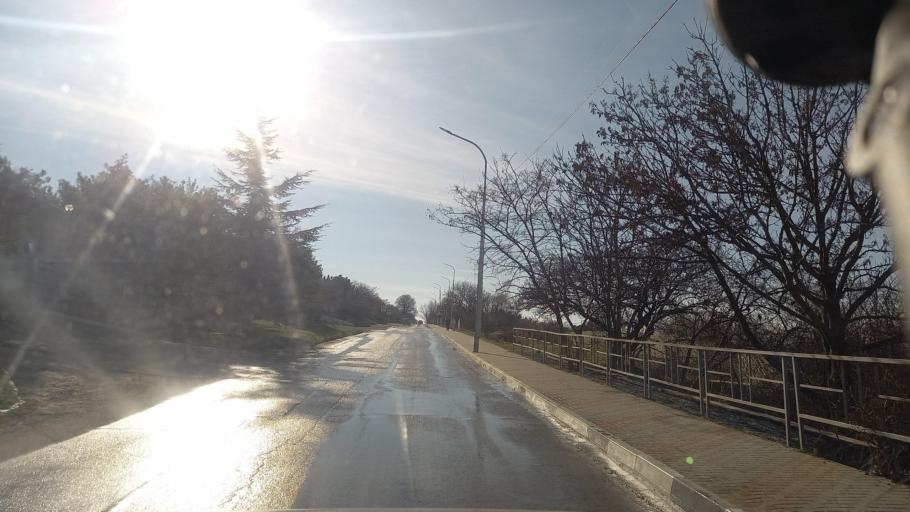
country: RU
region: Krasnodarskiy
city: Kabardinka
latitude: 44.6375
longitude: 37.9191
